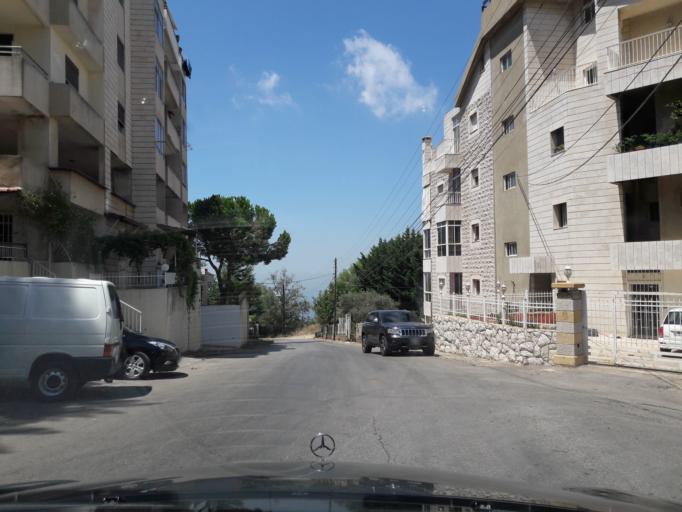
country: LB
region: Mont-Liban
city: Djounie
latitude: 33.9251
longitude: 35.6495
